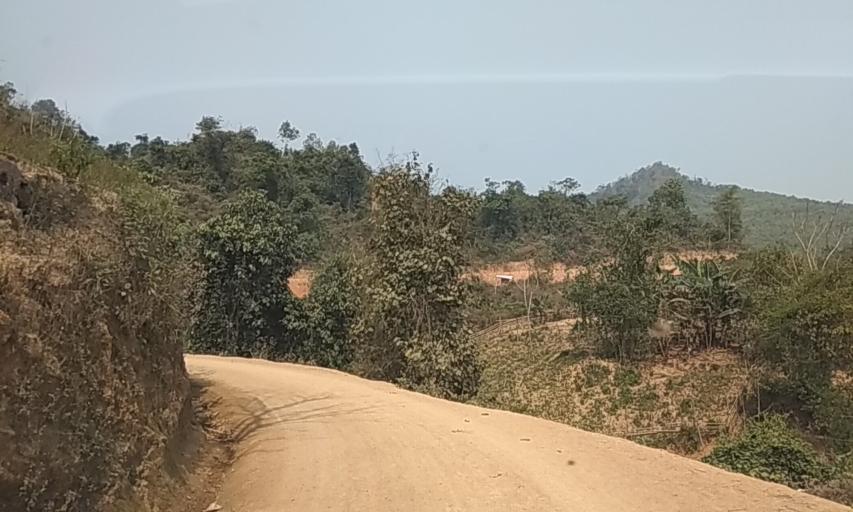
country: LA
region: Phongsali
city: Phongsali
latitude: 21.4771
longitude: 102.4431
